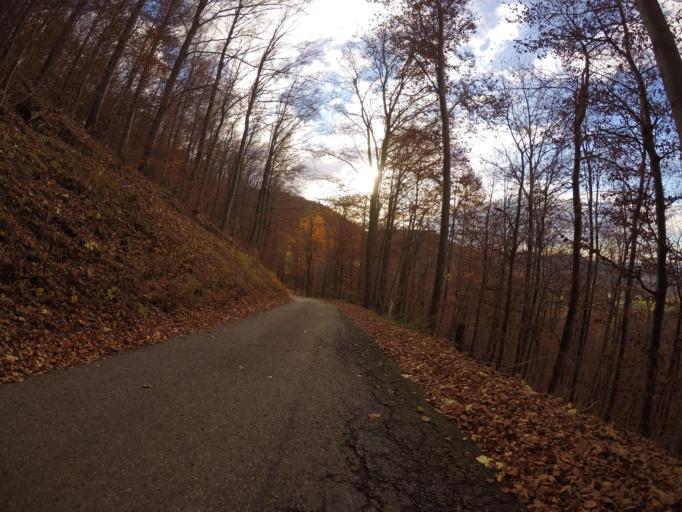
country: DE
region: Baden-Wuerttemberg
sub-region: Tuebingen Region
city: Eningen unter Achalm
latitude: 48.4710
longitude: 9.2987
